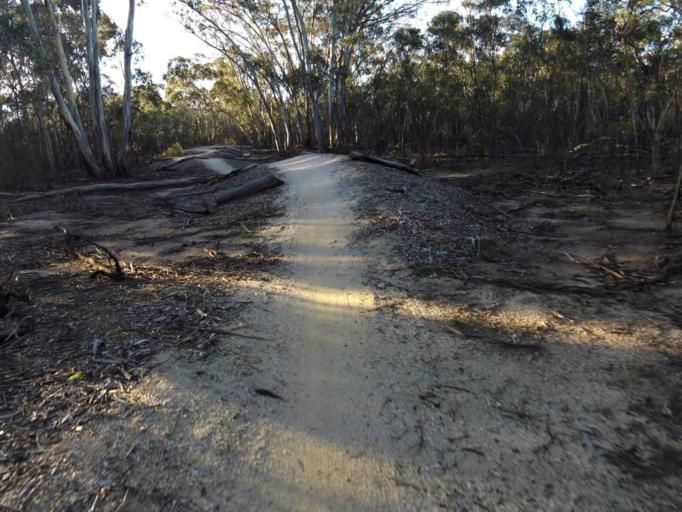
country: AU
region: Victoria
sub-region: Wyndham
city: Little River
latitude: -37.9632
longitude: 144.4399
